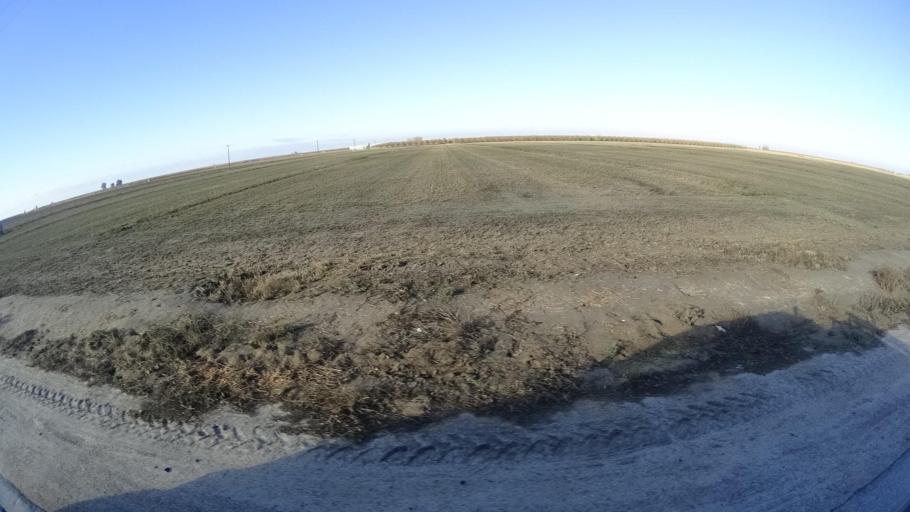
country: US
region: California
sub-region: Kern County
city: Delano
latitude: 35.7549
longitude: -119.3299
